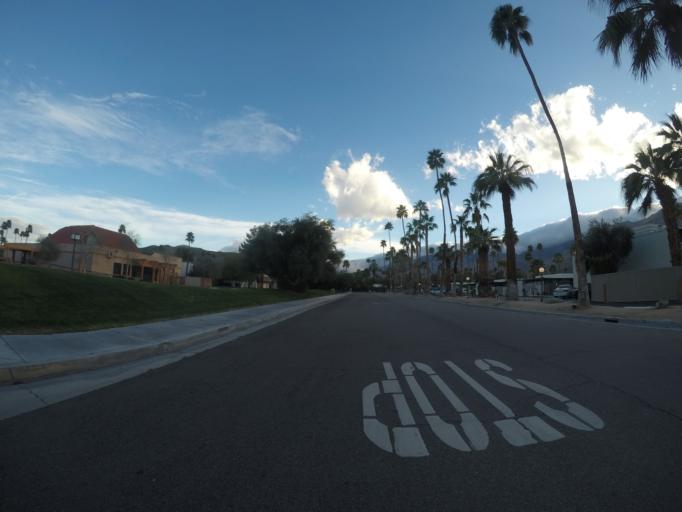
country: US
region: California
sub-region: Riverside County
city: Palm Springs
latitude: 33.8012
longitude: -116.5348
